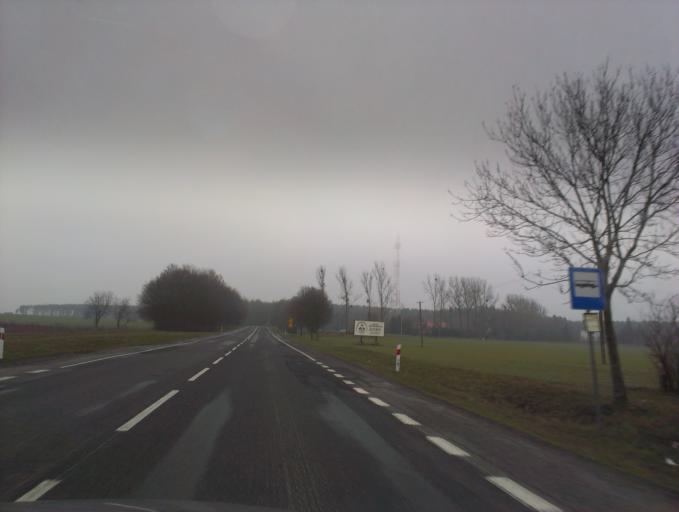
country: PL
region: Greater Poland Voivodeship
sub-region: Powiat pilski
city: Ujscie
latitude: 53.0333
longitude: 16.7809
